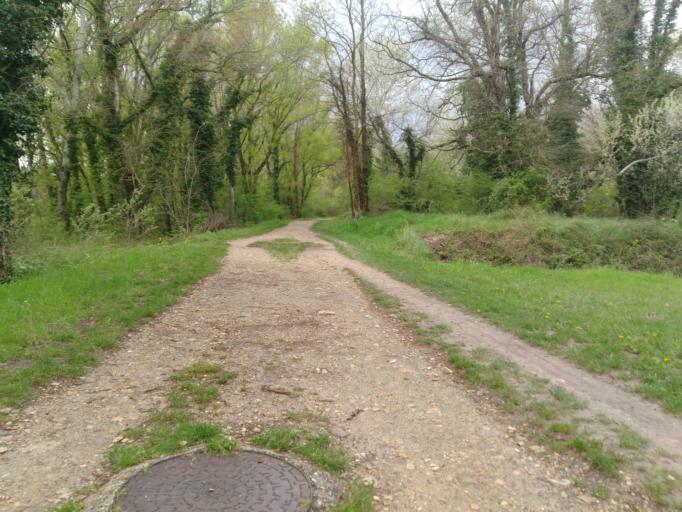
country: FR
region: Rhone-Alpes
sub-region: Departement de la Drome
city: Montboucher-sur-Jabron
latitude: 44.5448
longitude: 4.7799
